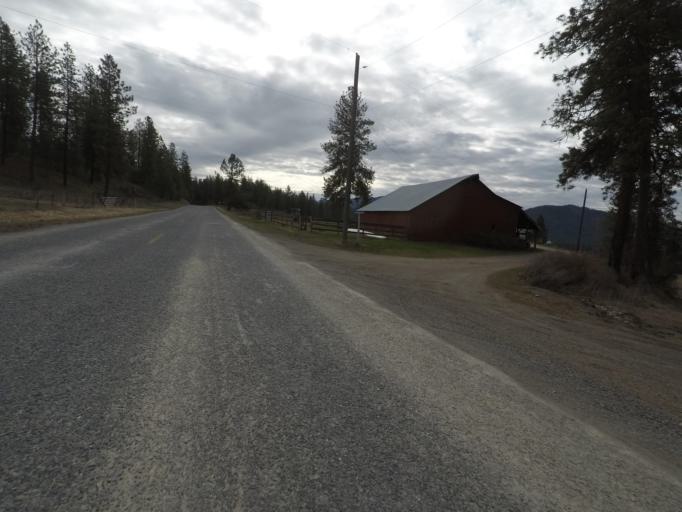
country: US
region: Washington
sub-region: Stevens County
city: Colville
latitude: 48.4990
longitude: -117.8417
